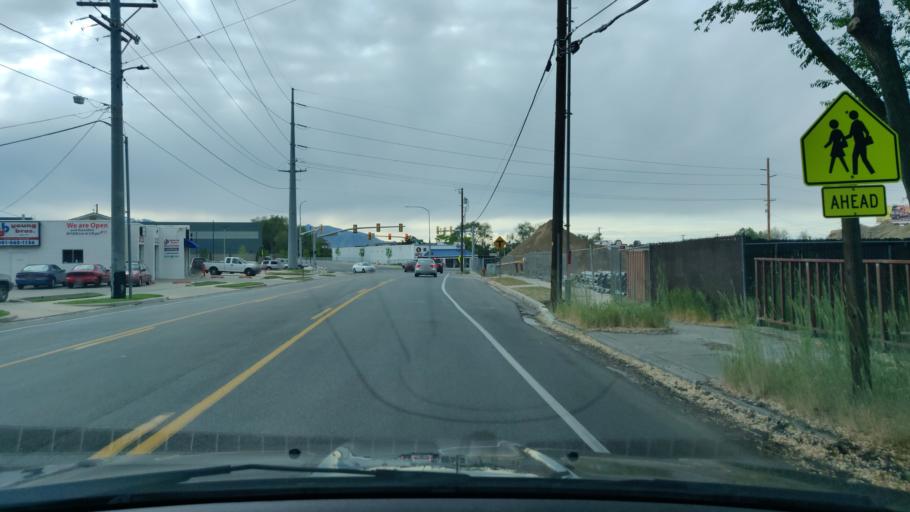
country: US
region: Utah
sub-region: Salt Lake County
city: Sandy City
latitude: 40.6197
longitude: -111.8646
